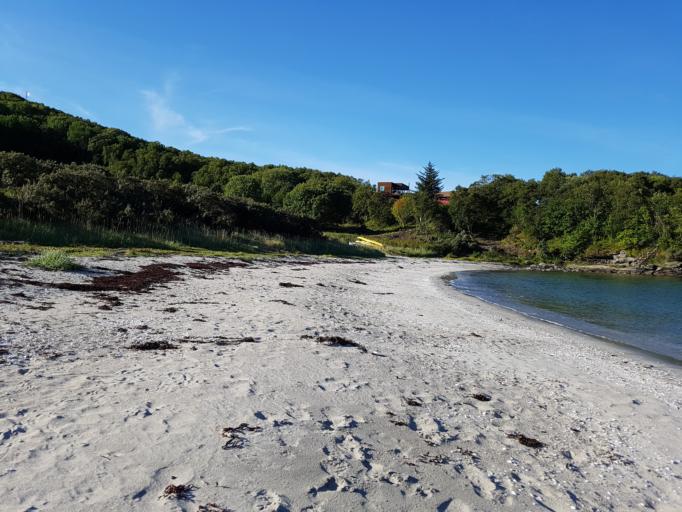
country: NO
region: Sor-Trondelag
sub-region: Afjord
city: A i Afjord
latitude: 64.0512
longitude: 9.9481
